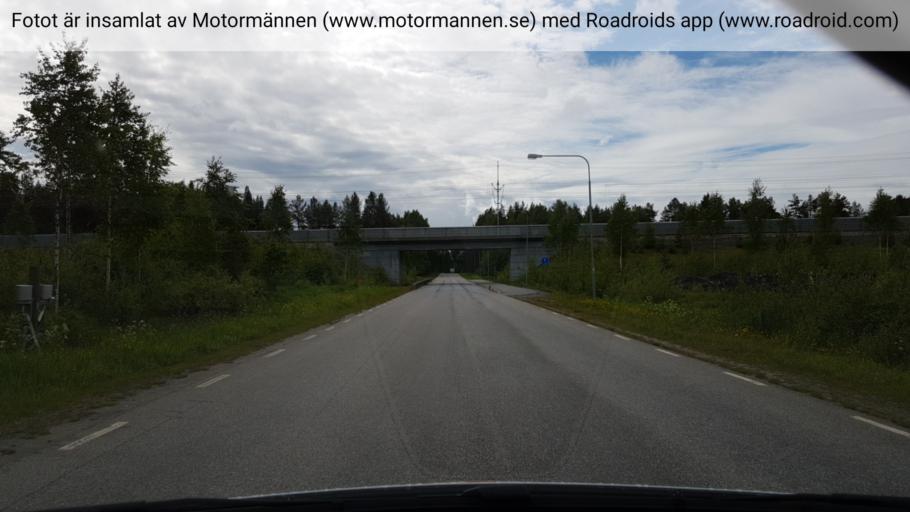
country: SE
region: Vaesterbotten
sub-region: Umea Kommun
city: Hoernefors
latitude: 63.6347
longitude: 19.9211
